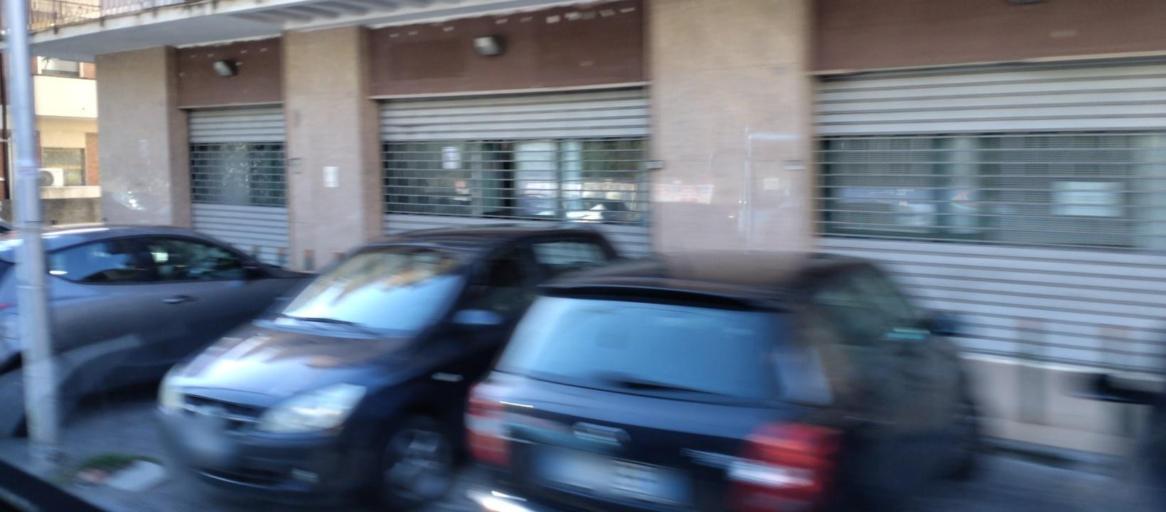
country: IT
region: Calabria
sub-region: Provincia di Catanzaro
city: Catanzaro
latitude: 38.8954
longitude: 16.6019
